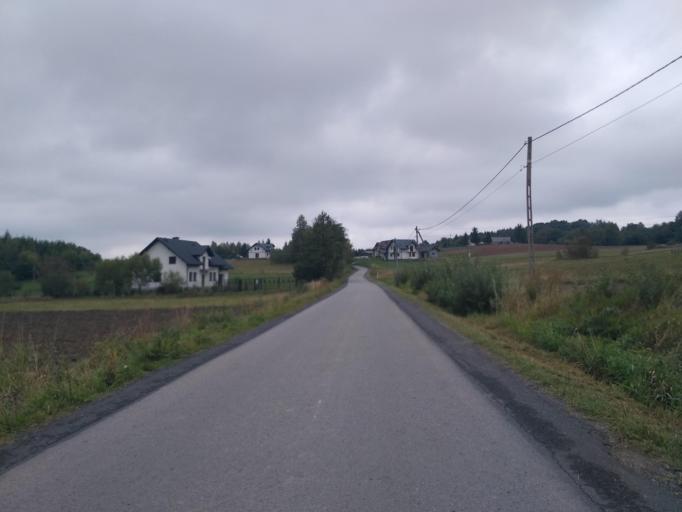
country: PL
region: Subcarpathian Voivodeship
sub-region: Powiat debicki
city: Brzostek
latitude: 49.9172
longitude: 21.4683
